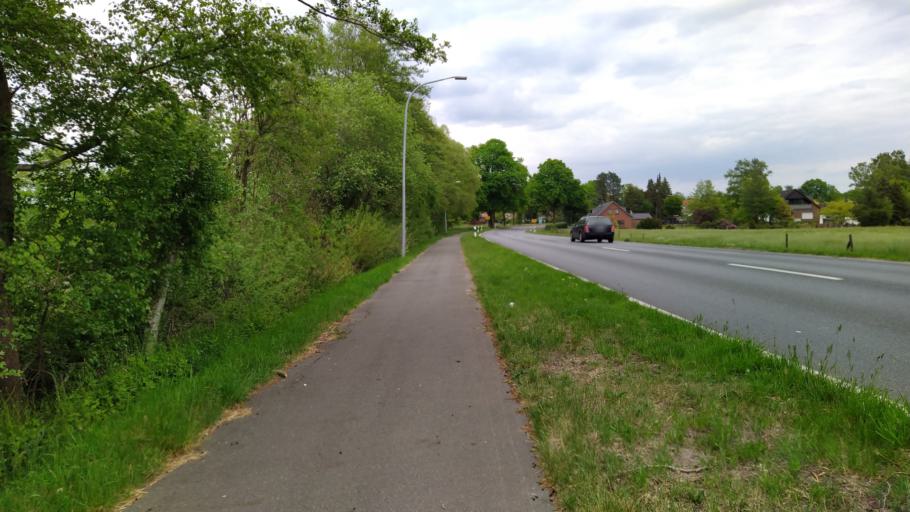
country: DE
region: Lower Saxony
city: Tarmstedt
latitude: 53.2175
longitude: 9.0579
